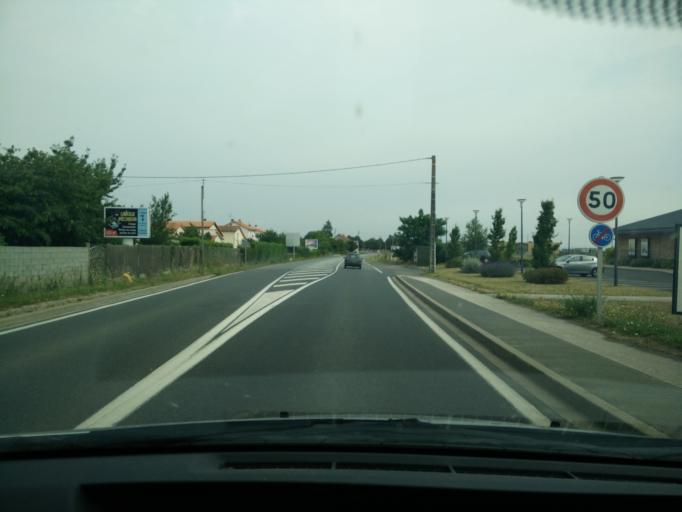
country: FR
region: Poitou-Charentes
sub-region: Departement des Deux-Sevres
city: Thouars
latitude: 46.9803
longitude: -0.1990
